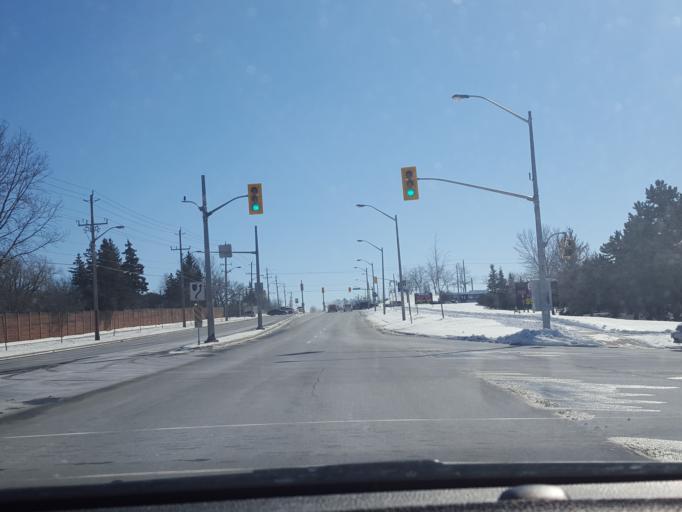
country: CA
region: Ontario
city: Kitchener
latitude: 43.4304
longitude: -80.5248
